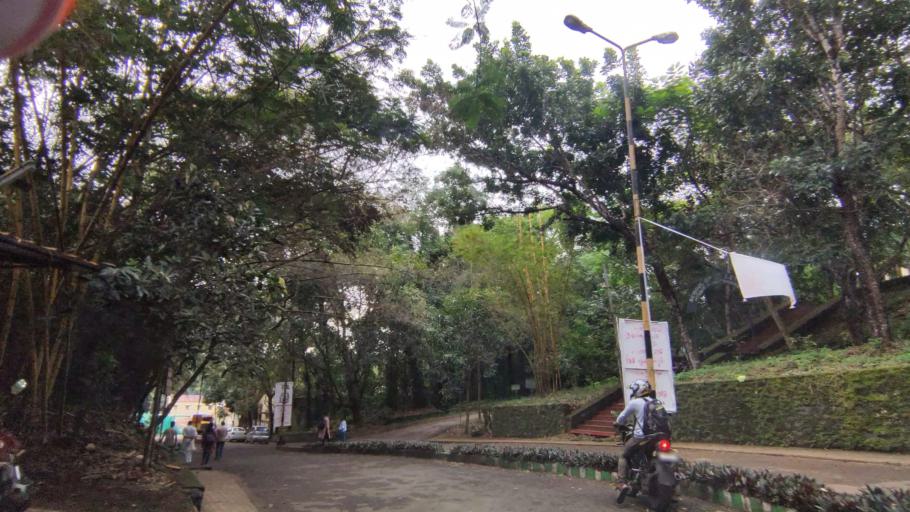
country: IN
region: Kerala
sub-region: Kottayam
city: Kottayam
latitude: 9.6595
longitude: 76.5319
